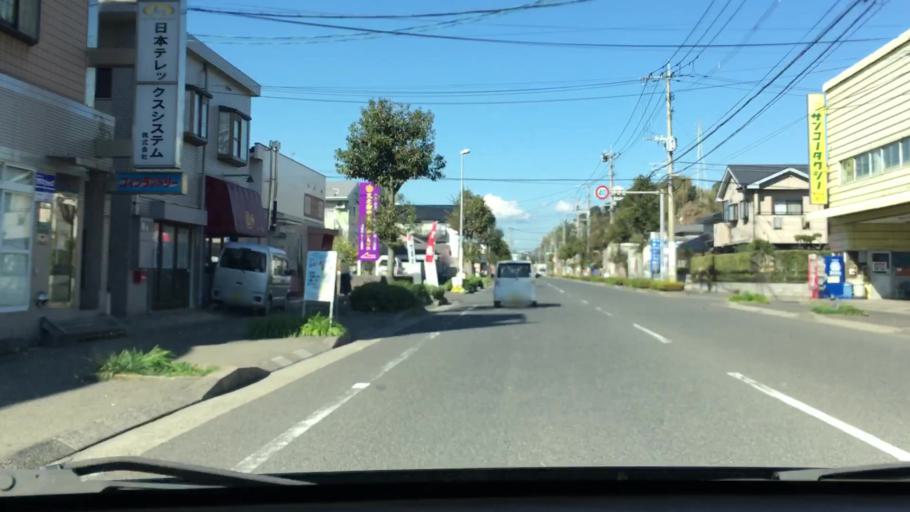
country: JP
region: Kagoshima
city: Kagoshima-shi
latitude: 31.5497
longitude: 130.5315
